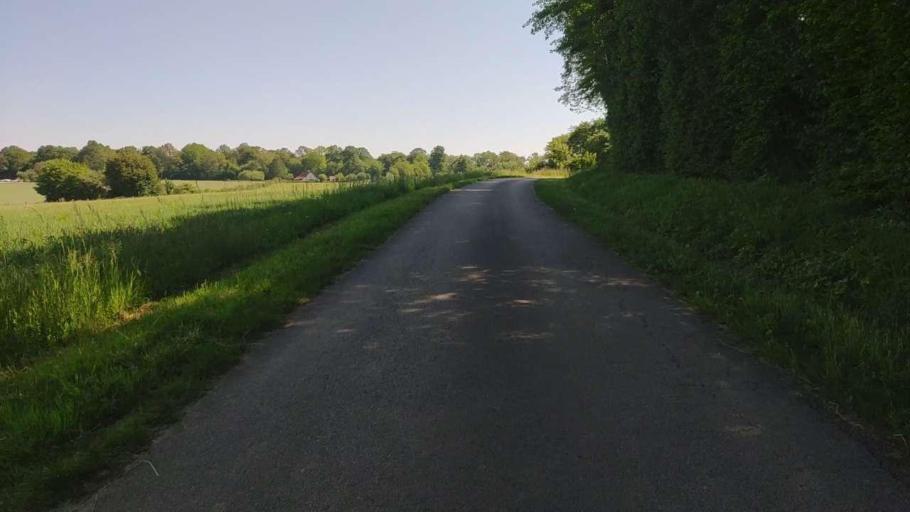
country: FR
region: Franche-Comte
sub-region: Departement du Jura
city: Bletterans
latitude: 46.7984
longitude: 5.4390
